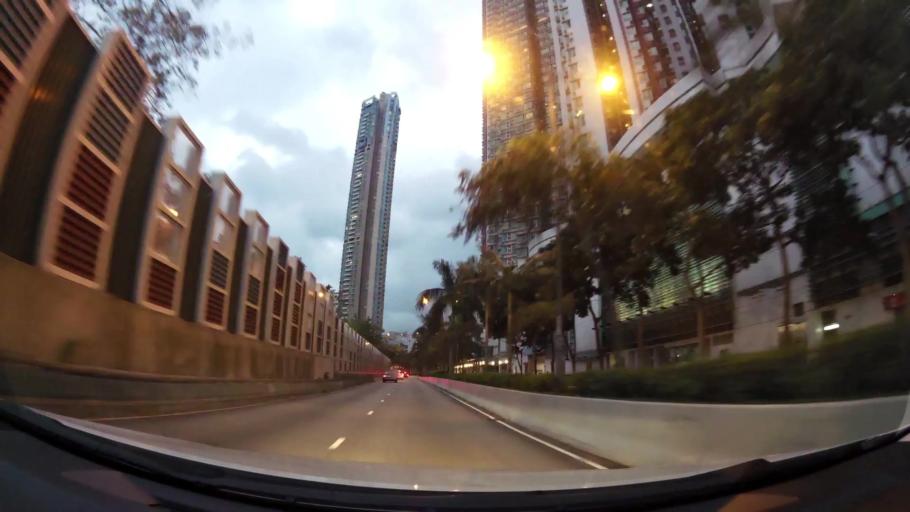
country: HK
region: Sham Shui Po
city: Sham Shui Po
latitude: 22.3249
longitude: 114.1596
